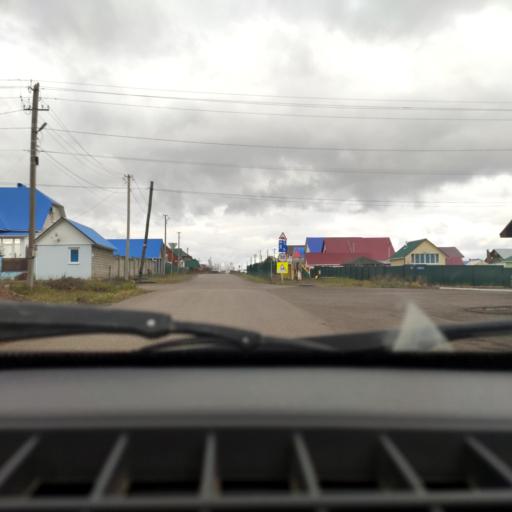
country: RU
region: Bashkortostan
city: Mikhaylovka
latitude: 54.8180
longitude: 55.8901
